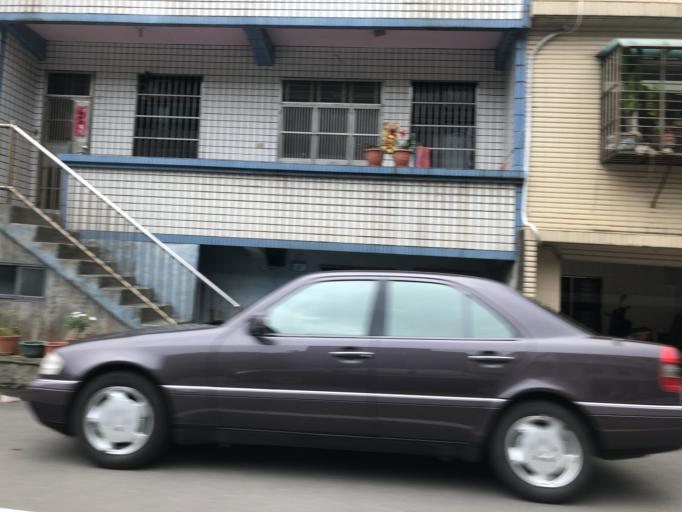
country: TW
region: Taiwan
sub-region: Keelung
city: Keelung
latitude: 25.2044
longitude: 121.6853
